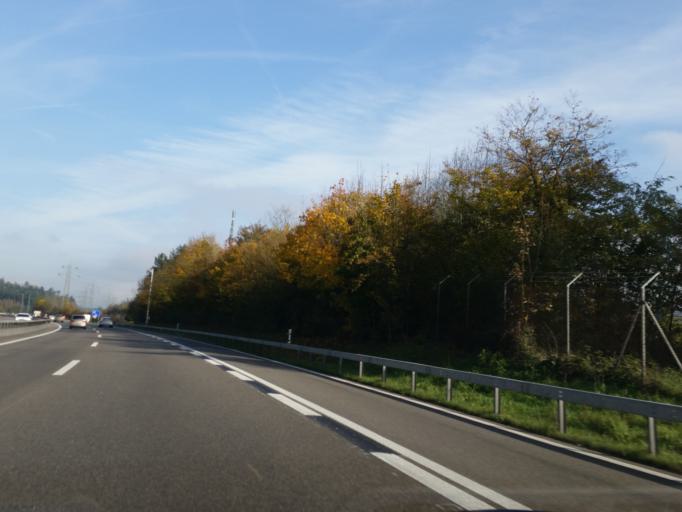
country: CH
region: Aargau
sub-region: Bezirk Lenzburg
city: Othmarsingen
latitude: 47.4006
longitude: 8.2049
